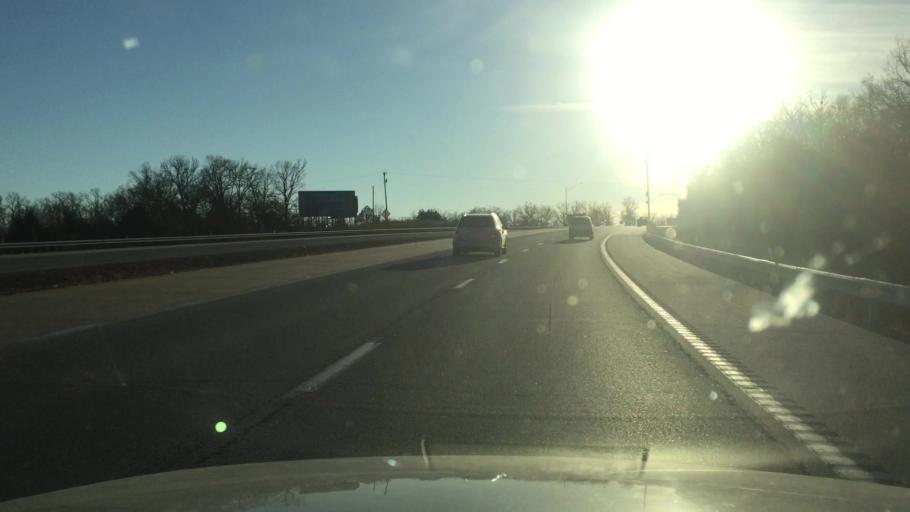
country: US
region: Missouri
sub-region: Cole County
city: Wardsville
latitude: 38.4752
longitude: -92.2763
